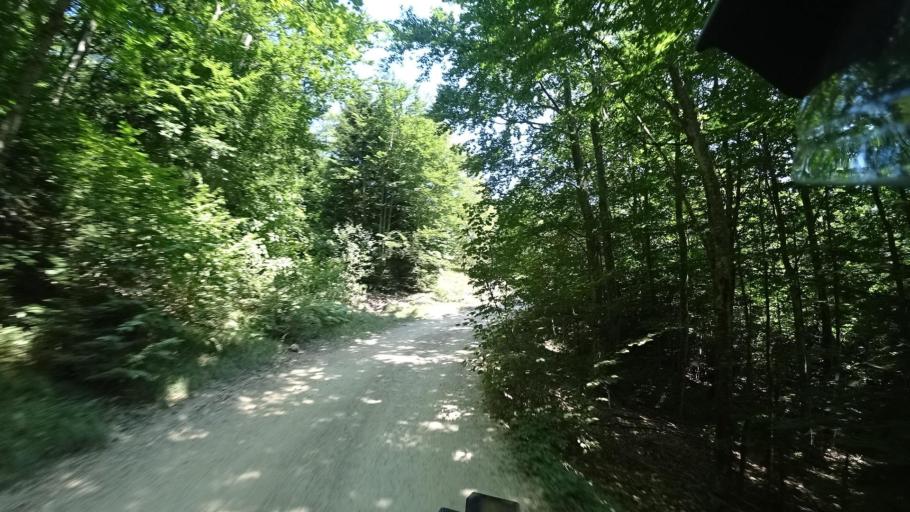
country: HR
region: Licko-Senjska
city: Popovaca
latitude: 44.5567
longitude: 15.2140
